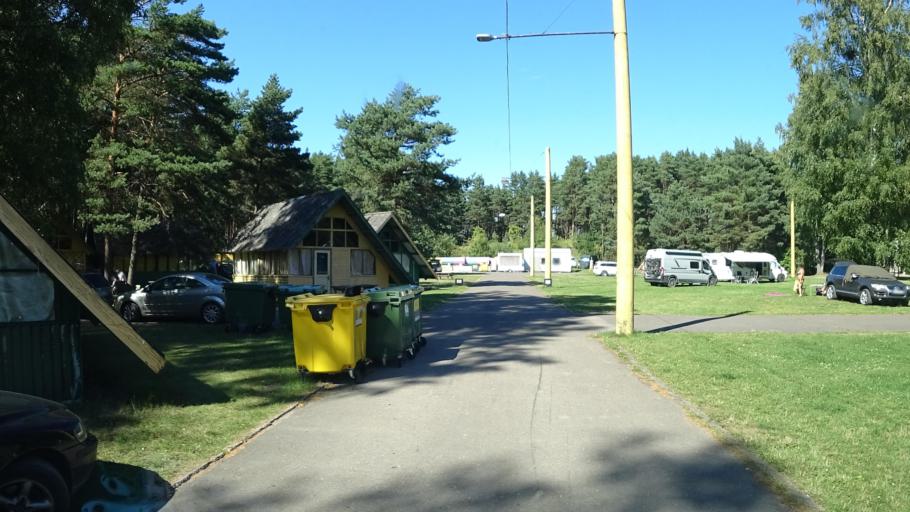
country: LV
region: Jurmala
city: Jurmala
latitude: 56.9603
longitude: 23.6453
